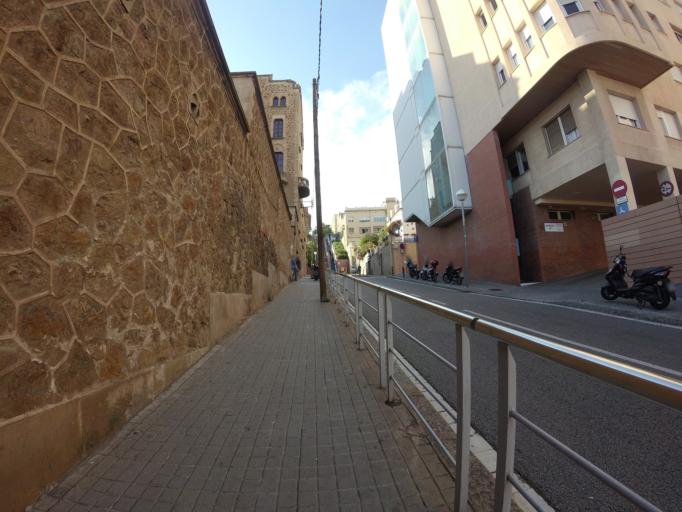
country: ES
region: Catalonia
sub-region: Provincia de Barcelona
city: Gracia
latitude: 41.4105
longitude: 2.1541
